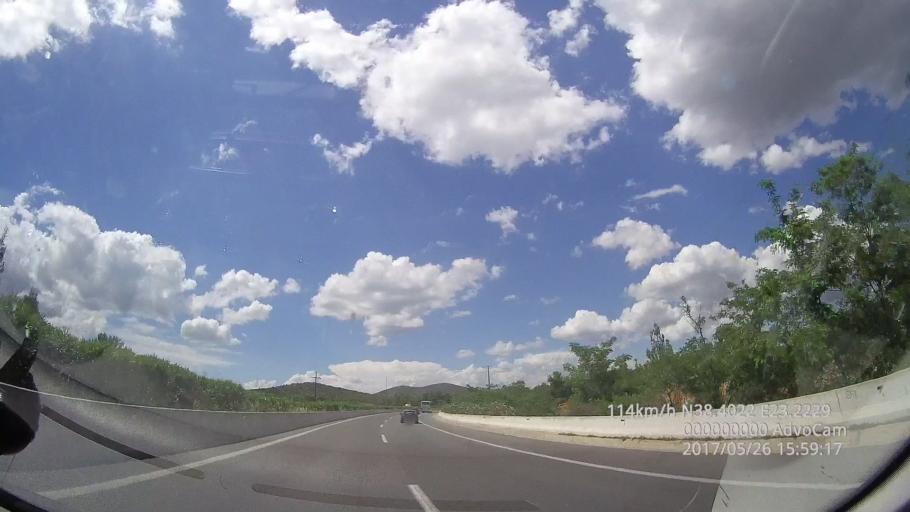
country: GR
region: Central Greece
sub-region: Nomos Fthiotidos
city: Ayios Konstandinos
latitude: 38.7644
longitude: 22.8398
